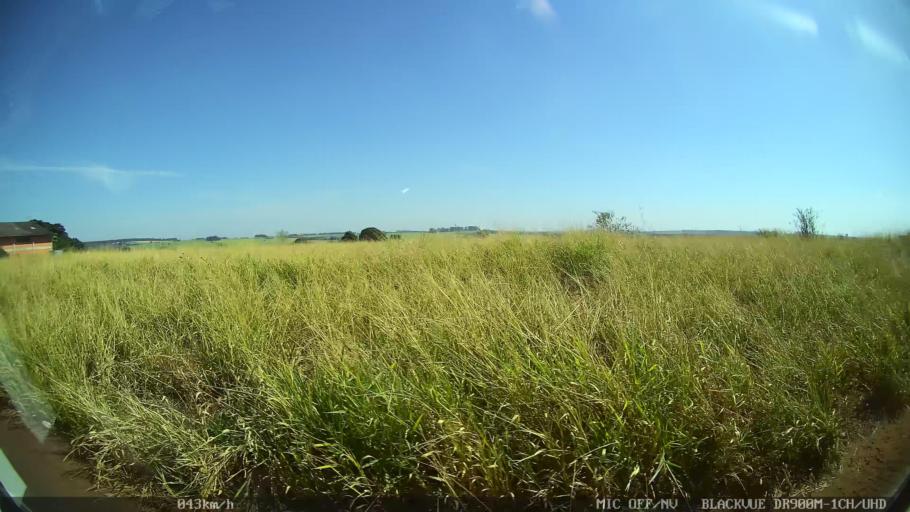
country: BR
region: Sao Paulo
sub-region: Batatais
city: Batatais
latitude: -20.8791
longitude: -47.6012
